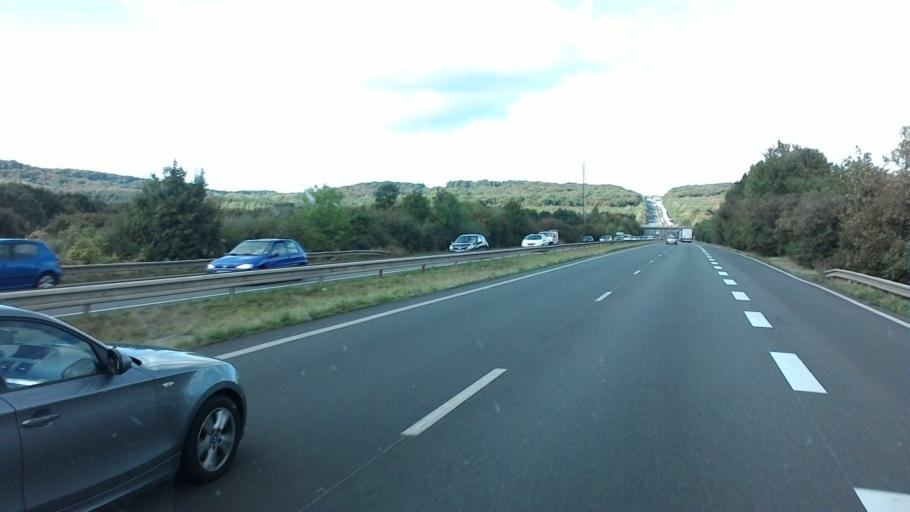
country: LU
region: Luxembourg
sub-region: Canton d'Esch-sur-Alzette
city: Dudelange
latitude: 49.4608
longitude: 6.1217
